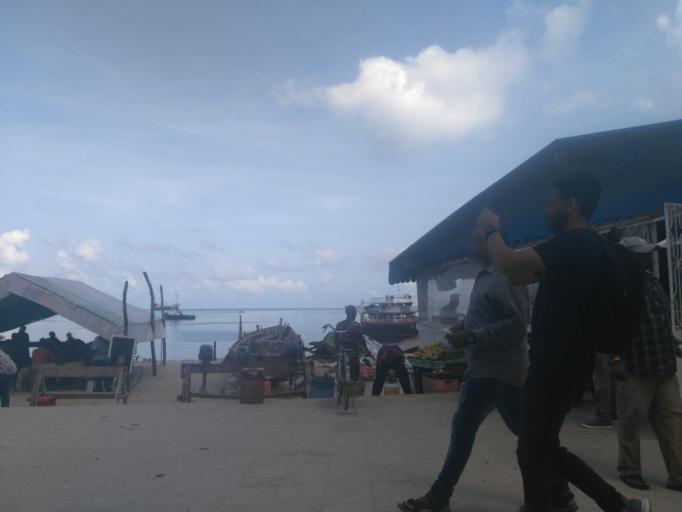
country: TZ
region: Zanzibar Urban/West
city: Zanzibar
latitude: -6.1585
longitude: 39.1919
